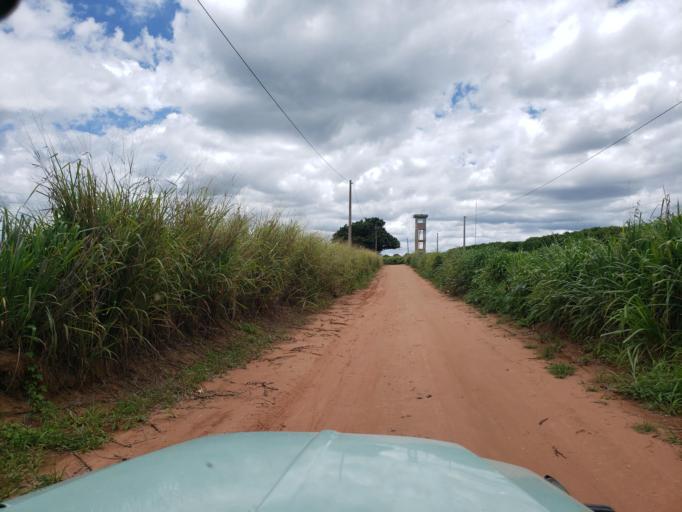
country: BR
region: Sao Paulo
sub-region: Moji-Guacu
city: Mogi-Gaucu
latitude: -22.2182
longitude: -46.8380
